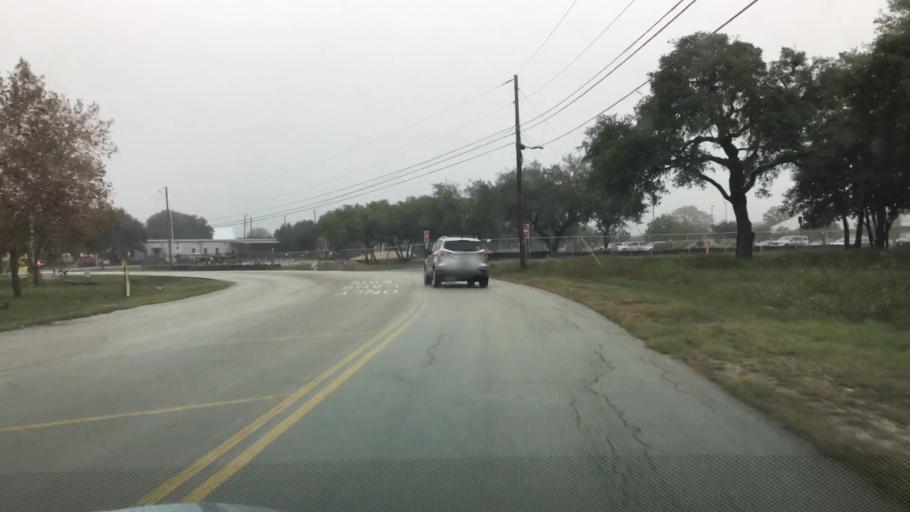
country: US
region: Texas
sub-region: Hays County
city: Dripping Springs
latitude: 30.1943
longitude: -98.0962
